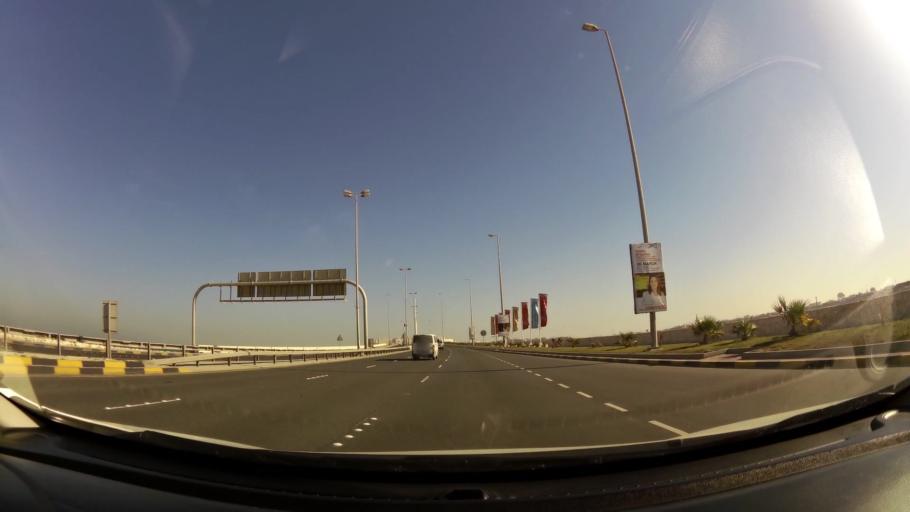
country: BH
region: Muharraq
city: Al Muharraq
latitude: 26.2498
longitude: 50.5922
